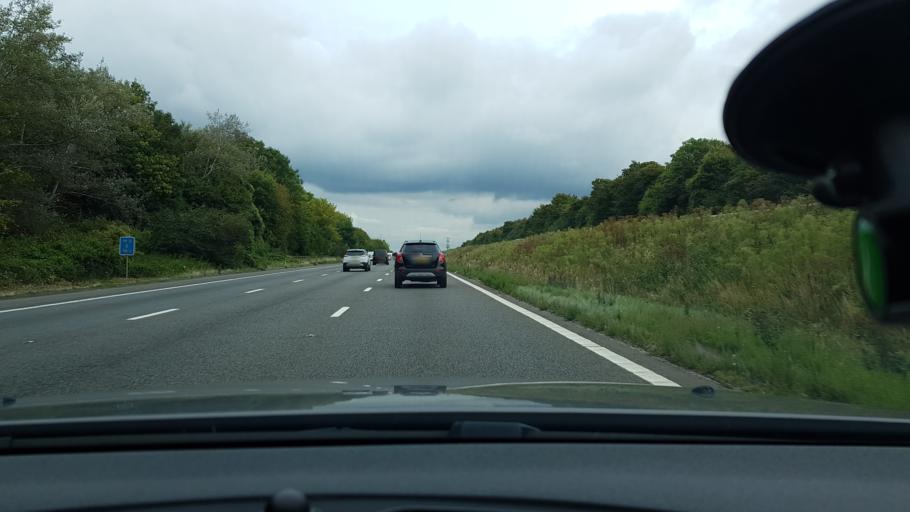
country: GB
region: England
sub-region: Hampshire
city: Basingstoke
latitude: 51.2405
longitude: -1.1036
